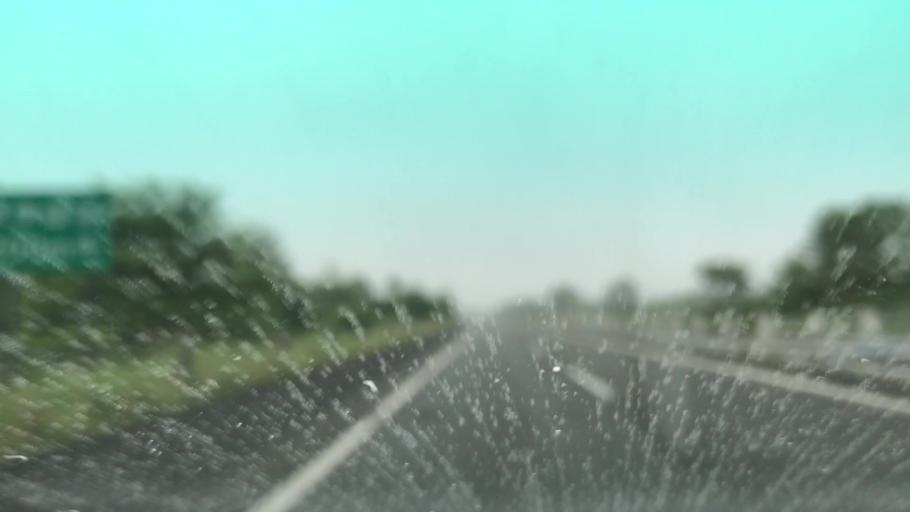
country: JP
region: Hokkaido
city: Shiraoi
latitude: 42.5227
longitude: 141.2689
